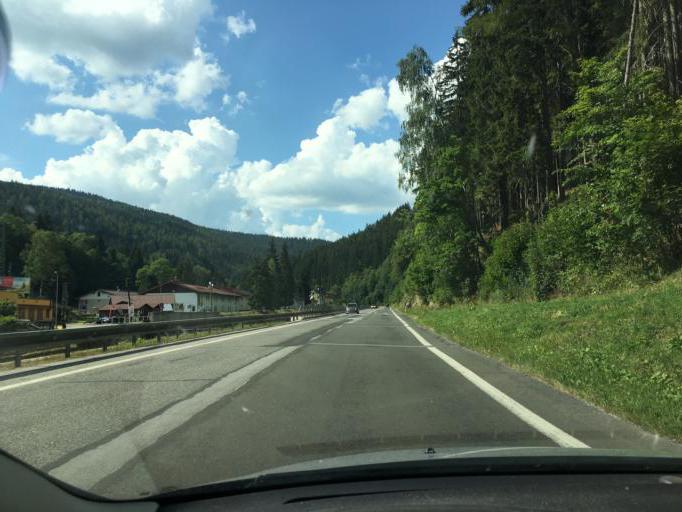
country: CZ
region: Kralovehradecky
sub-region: Okres Trutnov
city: Vrchlabi
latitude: 50.6579
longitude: 15.6003
